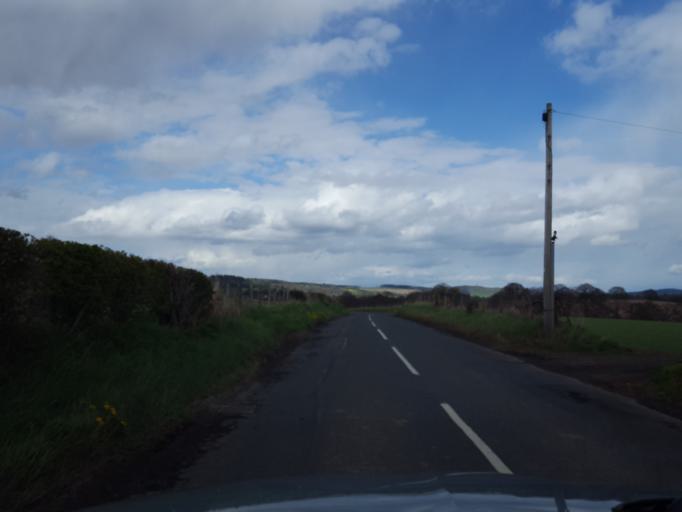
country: GB
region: Scotland
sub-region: Perth and Kinross
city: Methven
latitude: 56.3315
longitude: -3.5601
